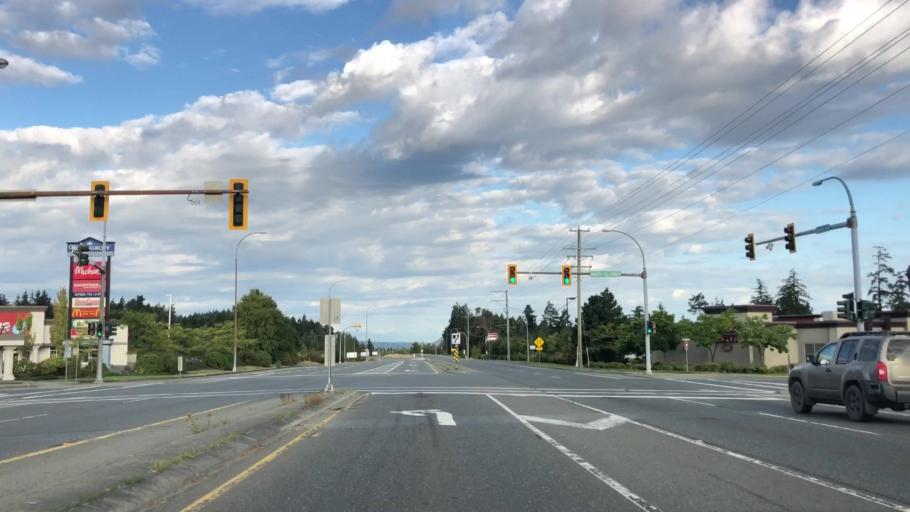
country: CA
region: British Columbia
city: Nanaimo
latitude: 49.2401
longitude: -124.0536
